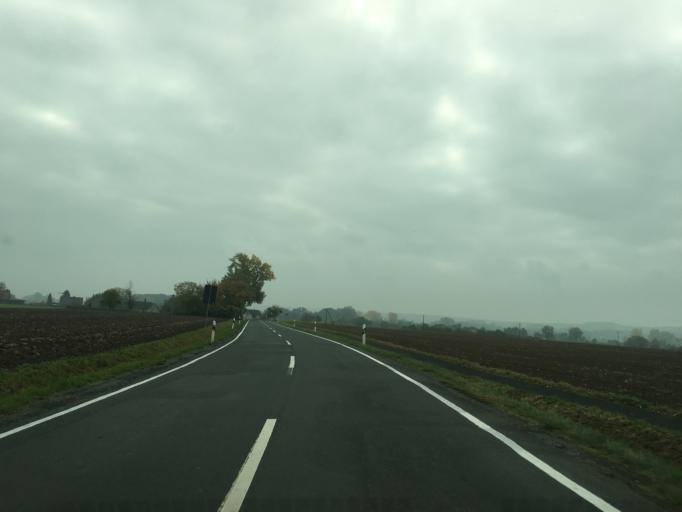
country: DE
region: North Rhine-Westphalia
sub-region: Regierungsbezirk Munster
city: Havixbeck
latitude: 51.9965
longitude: 7.3867
